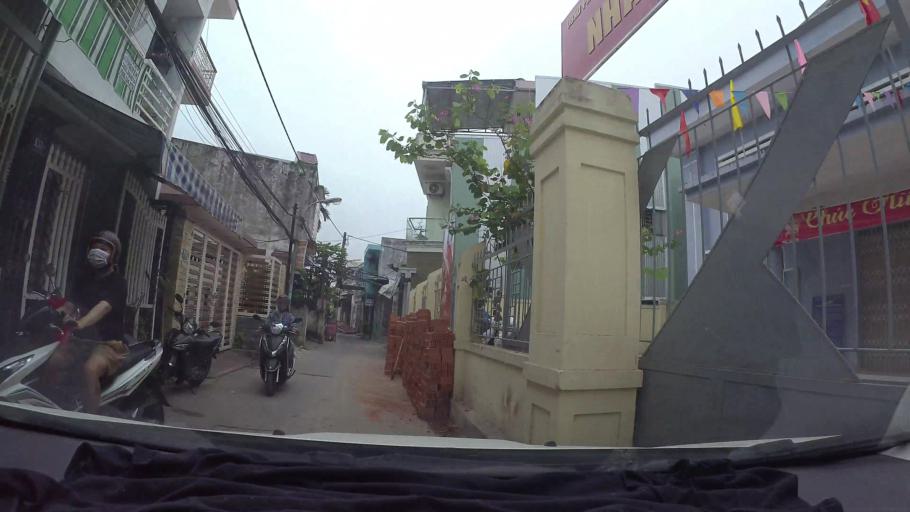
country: VN
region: Da Nang
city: Cam Le
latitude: 16.0299
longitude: 108.2237
